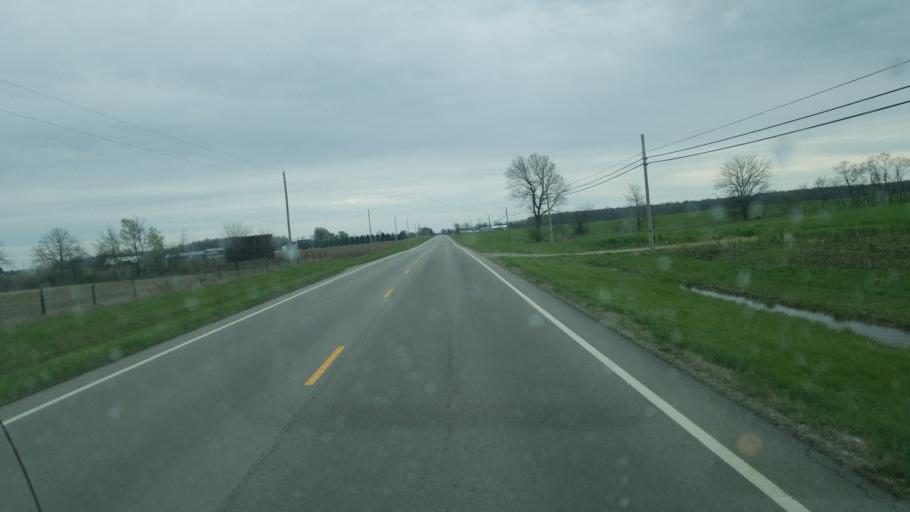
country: US
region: Ohio
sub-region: Hardin County
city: Kenton
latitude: 40.6442
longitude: -83.5439
